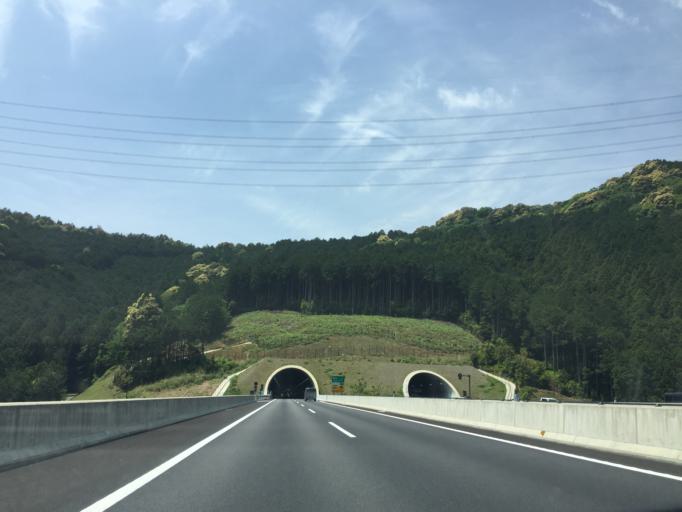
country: JP
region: Aichi
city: Shinshiro
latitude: 34.9038
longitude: 137.4504
